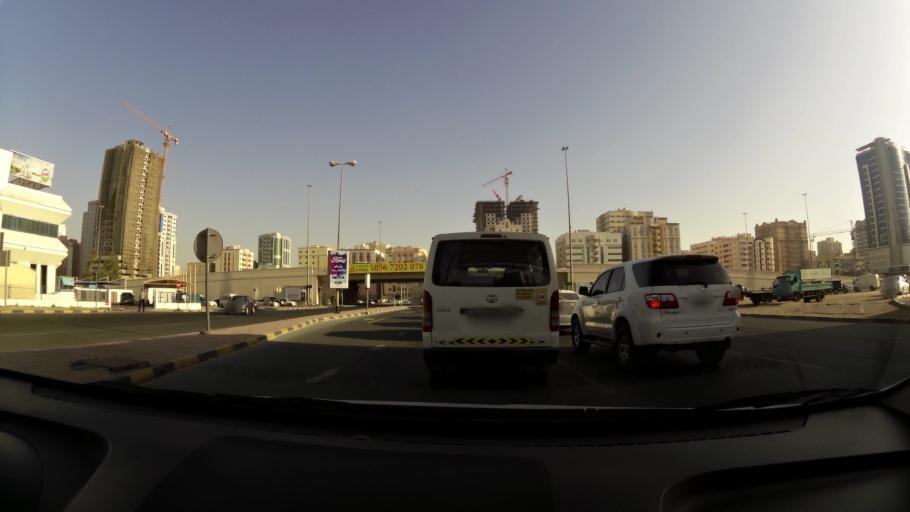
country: AE
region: Ajman
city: Ajman
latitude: 25.3908
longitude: 55.4550
